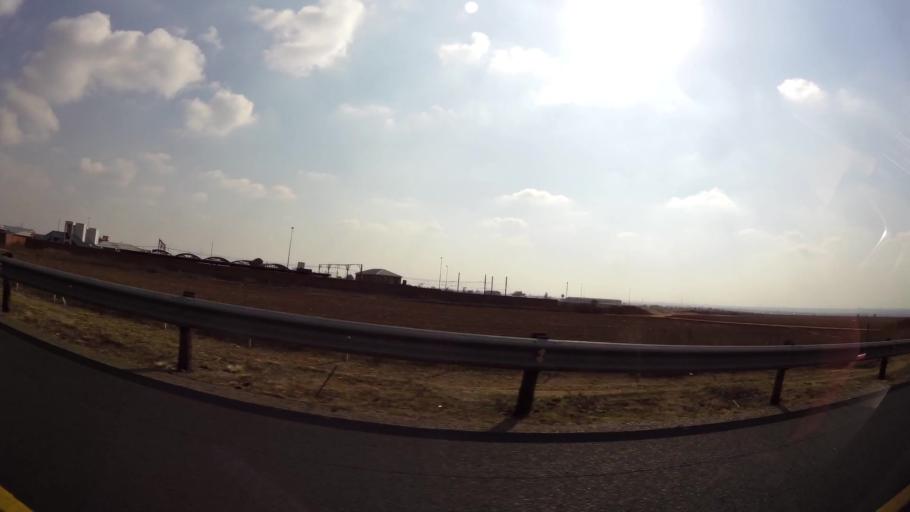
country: ZA
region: Gauteng
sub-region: Ekurhuleni Metropolitan Municipality
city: Springs
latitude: -26.1573
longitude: 28.4259
